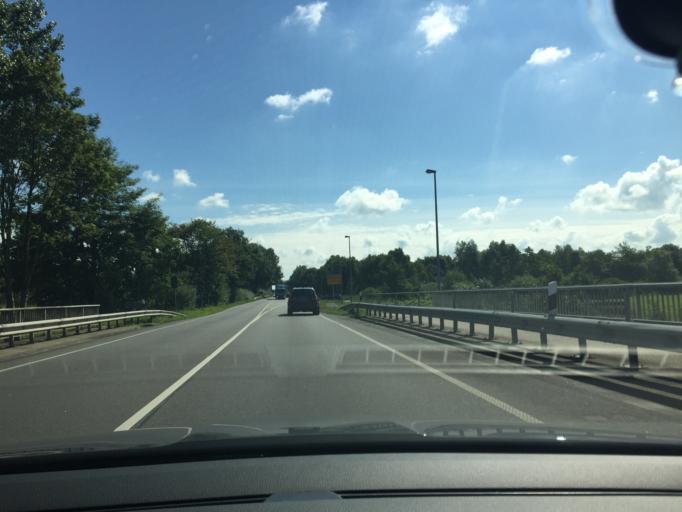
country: DE
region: Lower Saxony
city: Wittmund
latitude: 53.5761
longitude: 7.7962
